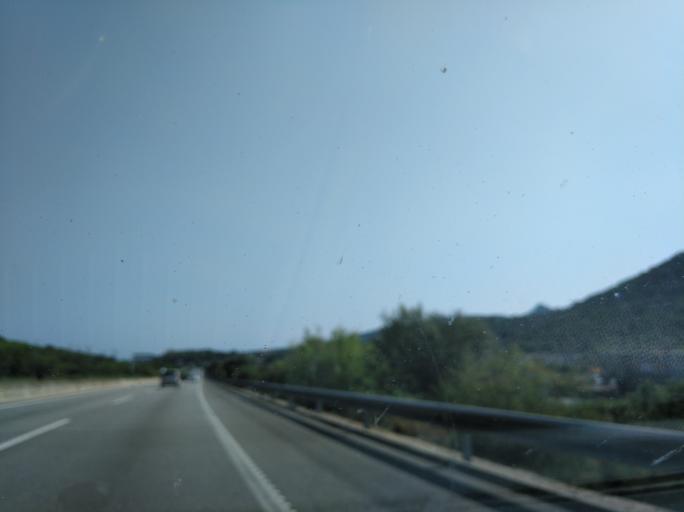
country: ES
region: Catalonia
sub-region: Provincia de Barcelona
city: Argentona
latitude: 41.5696
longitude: 2.3949
